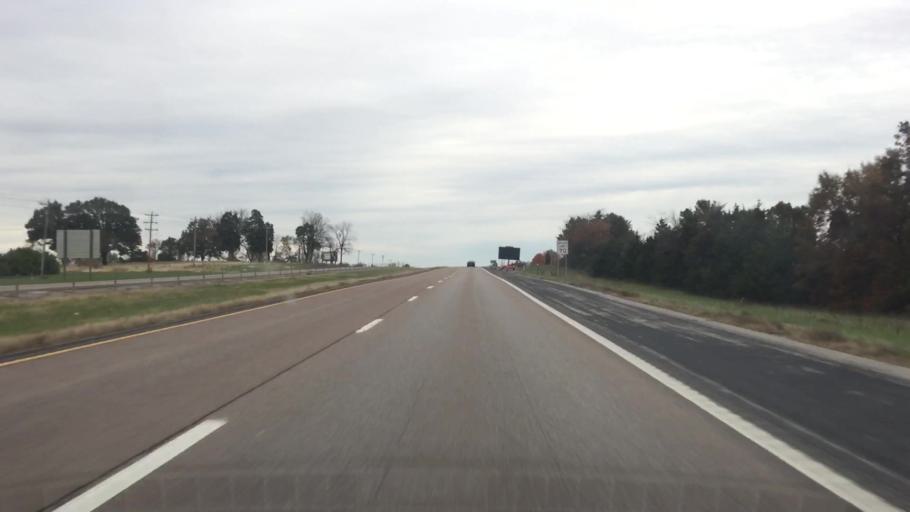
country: US
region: Missouri
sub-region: Boone County
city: Ashland
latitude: 38.7821
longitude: -92.2522
